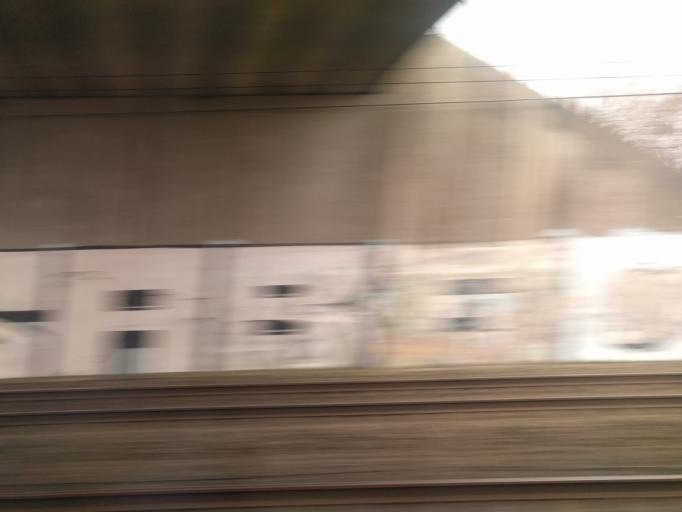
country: DK
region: Capital Region
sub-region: Hoje-Taastrup Kommune
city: Flong
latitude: 55.6493
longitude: 12.1594
